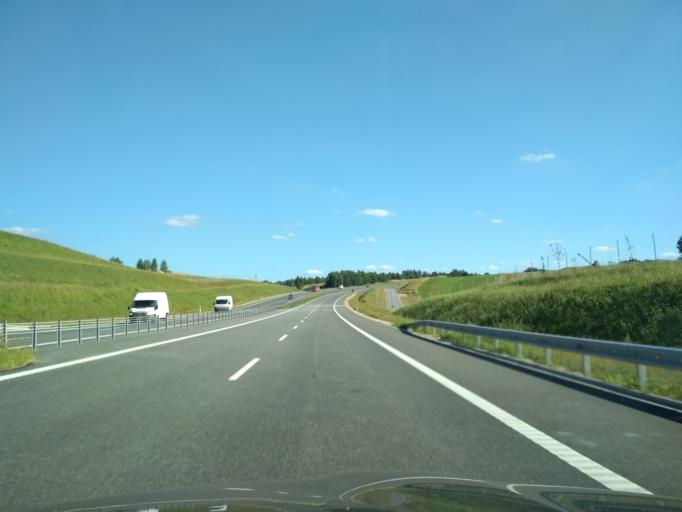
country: PL
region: Subcarpathian Voivodeship
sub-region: Rzeszow
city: Przybyszowka
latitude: 50.0459
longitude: 21.9313
